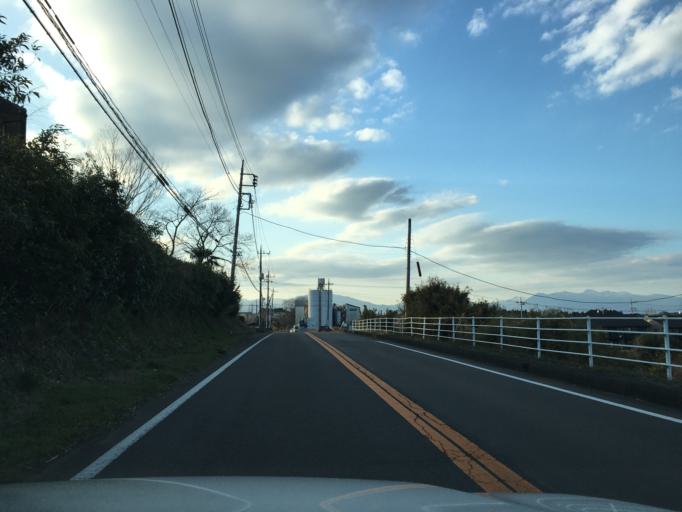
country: JP
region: Tochigi
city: Otawara
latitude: 36.8657
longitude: 140.0815
